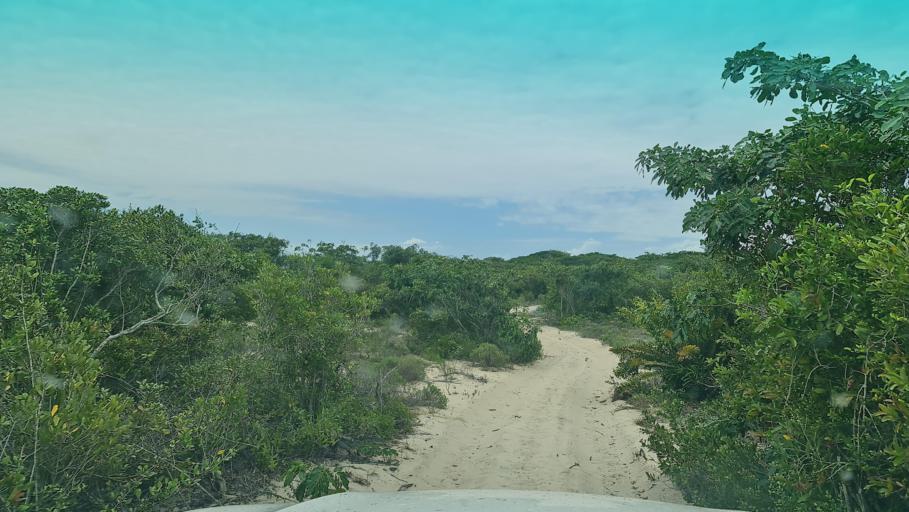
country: MZ
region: Maputo
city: Manhica
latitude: -25.6375
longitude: 32.7838
